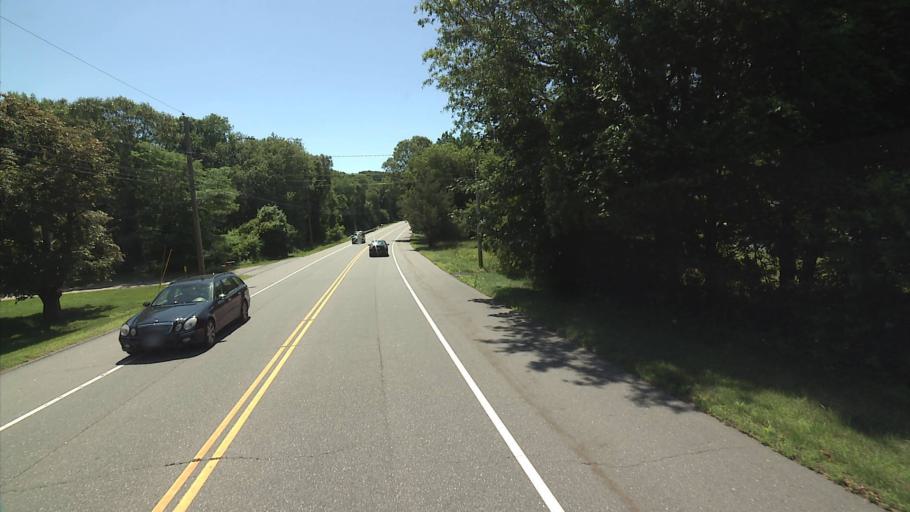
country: US
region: Connecticut
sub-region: New London County
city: Noank
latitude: 41.3371
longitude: -72.0044
